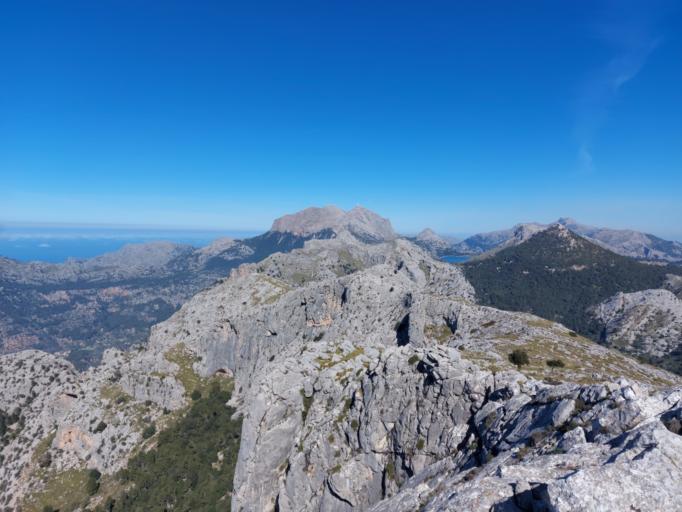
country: ES
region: Balearic Islands
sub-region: Illes Balears
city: Soller
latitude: 39.7510
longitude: 2.7425
